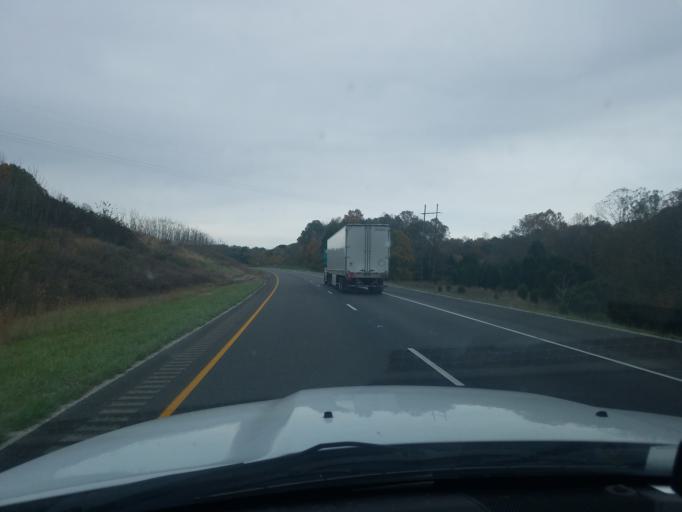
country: US
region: Indiana
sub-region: Crawford County
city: English
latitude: 38.2382
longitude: -86.4774
